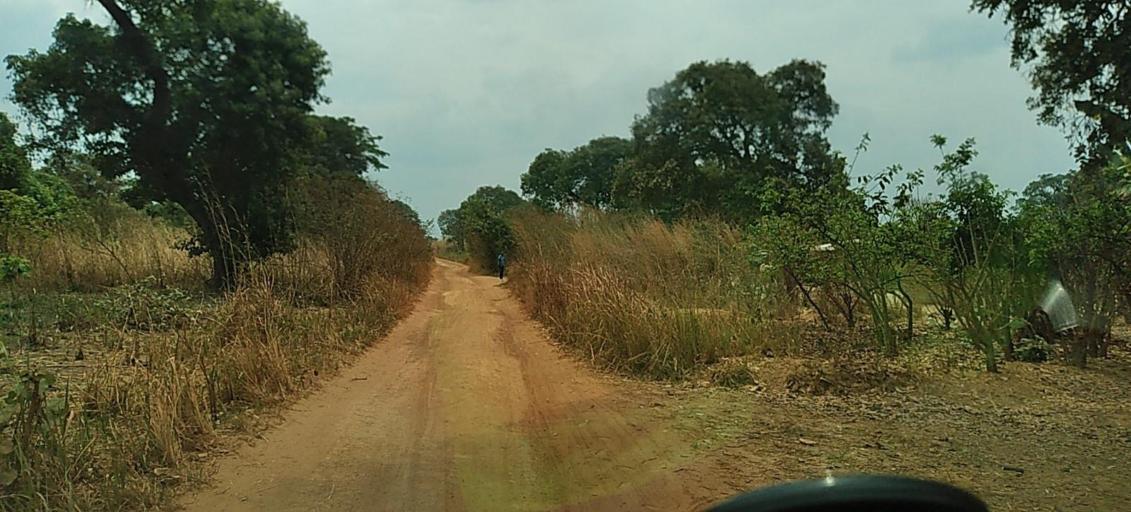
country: ZM
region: North-Western
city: Kansanshi
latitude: -12.0584
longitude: 26.3470
